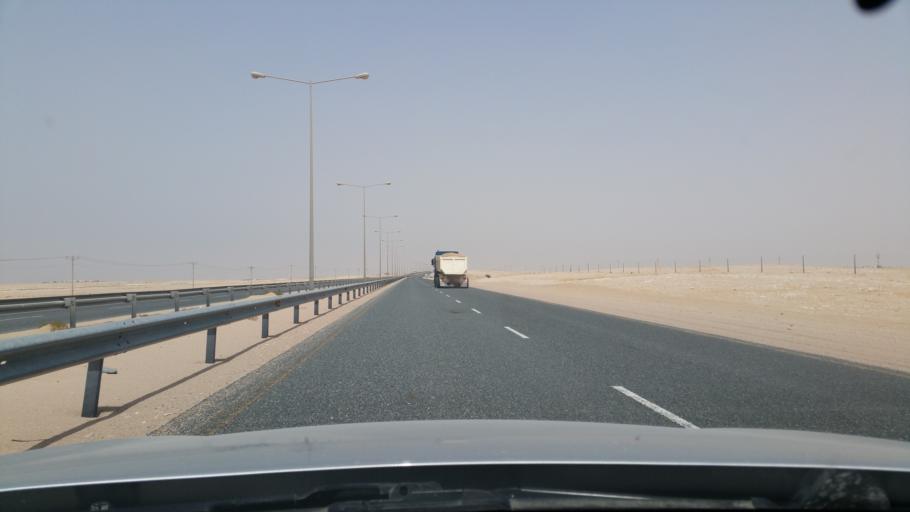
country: QA
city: Umm Bab
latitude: 25.0090
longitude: 50.9158
